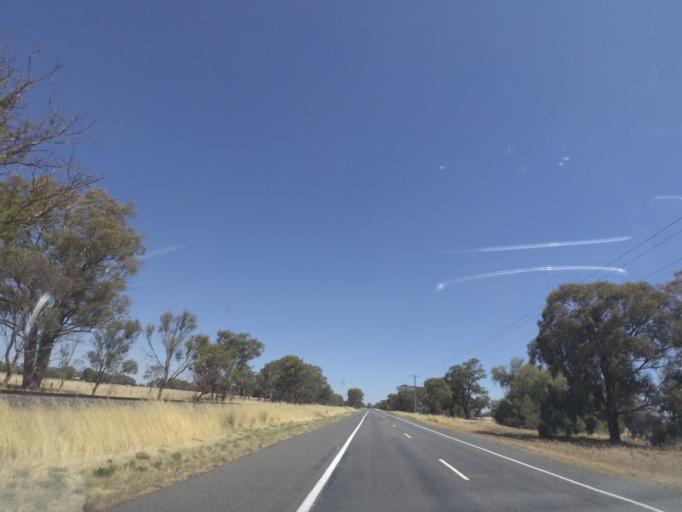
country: AU
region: Victoria
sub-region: Greater Shepparton
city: Shepparton
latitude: -36.2150
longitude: 145.4318
